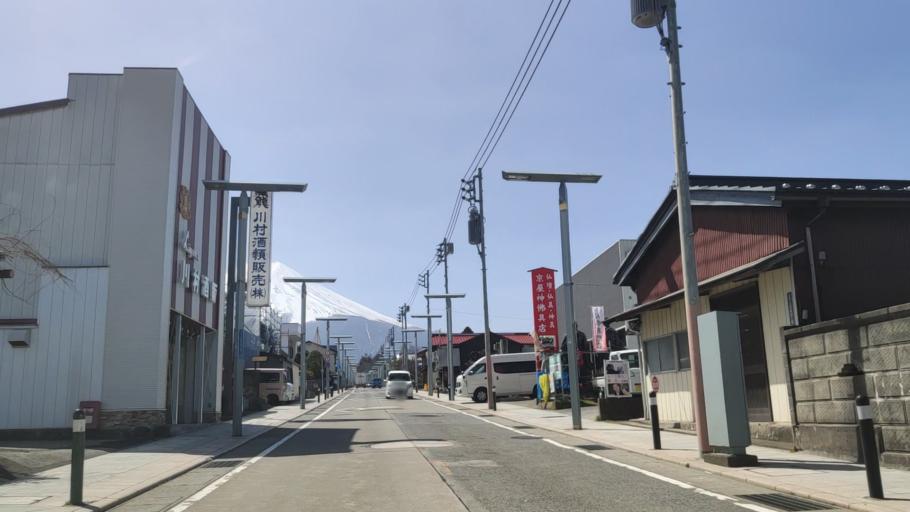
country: JP
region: Yamanashi
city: Fujikawaguchiko
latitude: 35.4801
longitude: 138.7956
